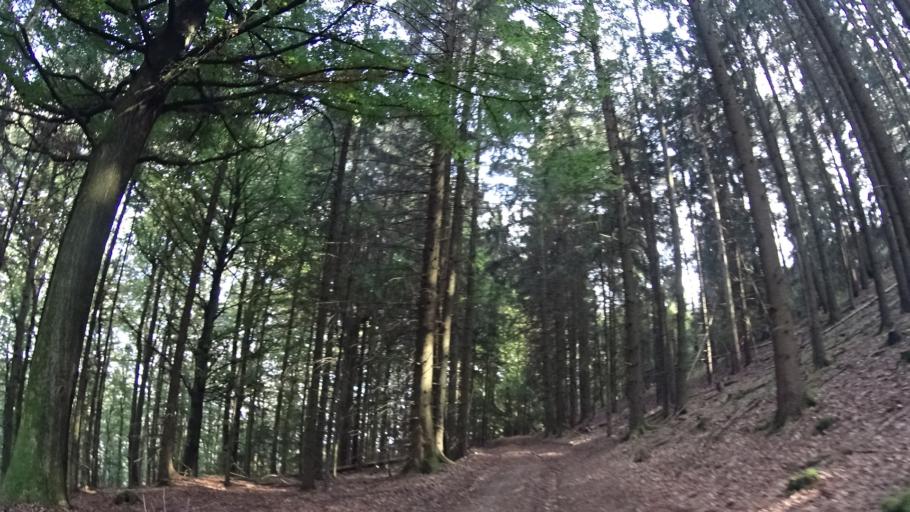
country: DE
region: Bavaria
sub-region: Lower Bavaria
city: Riedenburg
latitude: 48.9842
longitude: 11.6791
